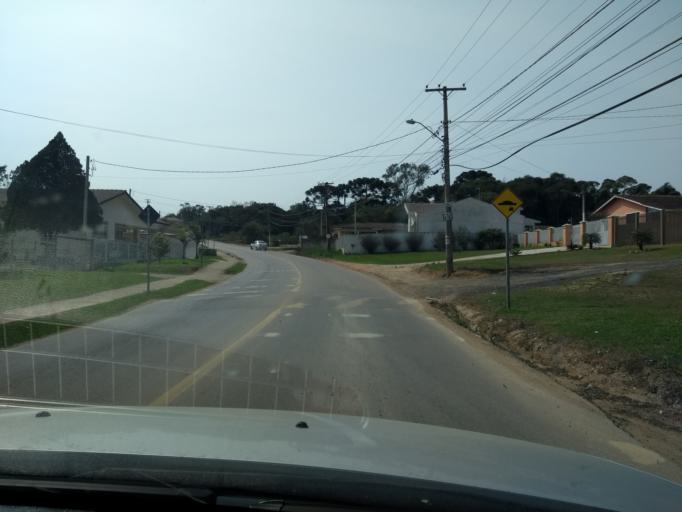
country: BR
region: Parana
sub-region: Araucaria
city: Araucaria
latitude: -25.6113
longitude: -49.3372
